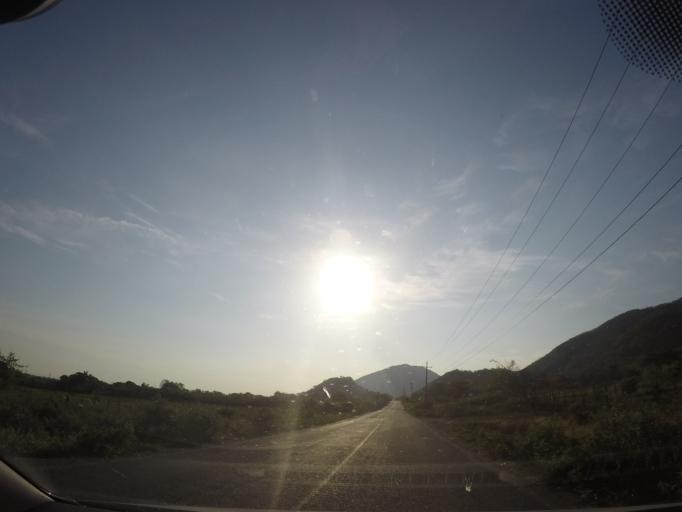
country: MX
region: Oaxaca
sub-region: Santo Domingo Tehuantepec
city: La Noria
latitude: 16.2349
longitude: -95.1710
